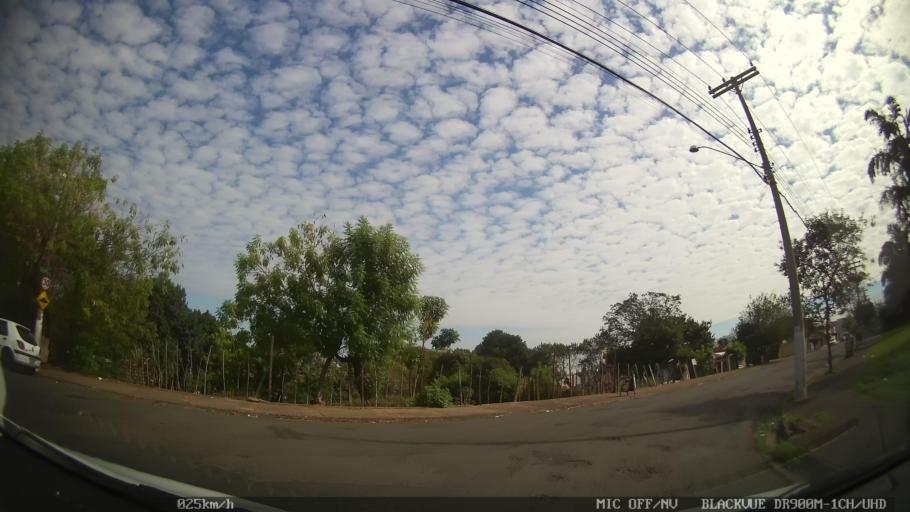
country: BR
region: Sao Paulo
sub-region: Santa Barbara D'Oeste
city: Santa Barbara d'Oeste
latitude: -22.7720
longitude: -47.3894
